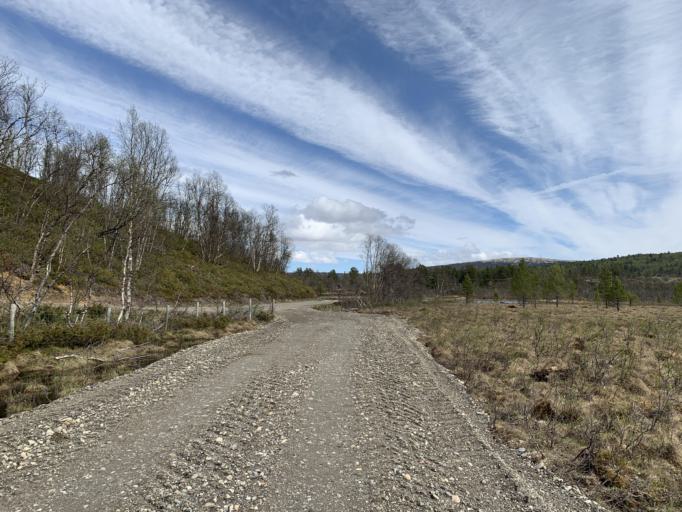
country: NO
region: Hedmark
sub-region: Alvdal
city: Alvdal
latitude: 62.4130
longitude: 10.4033
